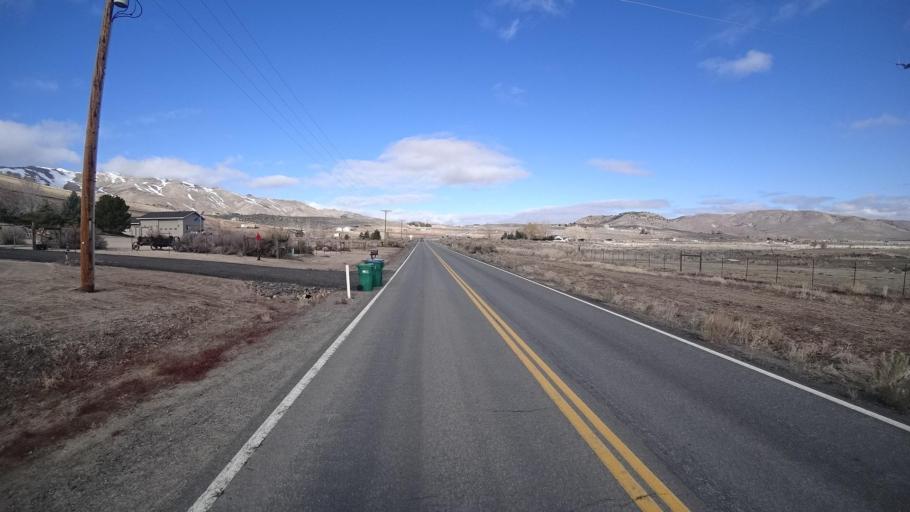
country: US
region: Nevada
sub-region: Washoe County
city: Cold Springs
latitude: 39.8614
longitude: -119.9380
